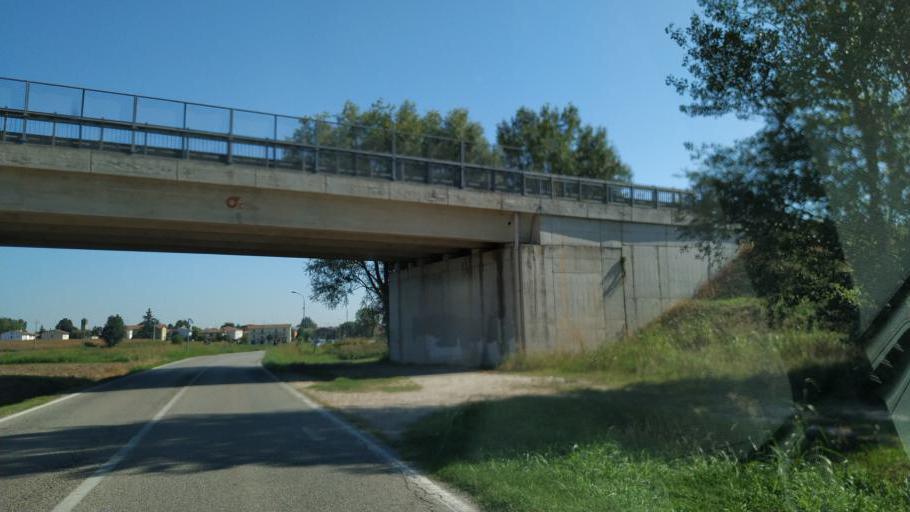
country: IT
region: Emilia-Romagna
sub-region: Provincia di Ferrara
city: San Carlo
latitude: 44.7992
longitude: 11.4041
